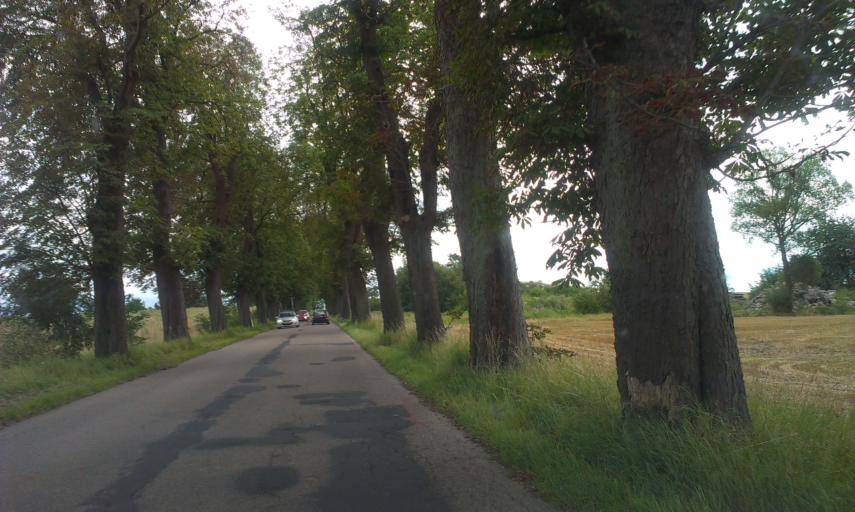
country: PL
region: West Pomeranian Voivodeship
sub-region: Powiat szczecinecki
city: Barwice
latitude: 53.7338
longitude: 16.3551
